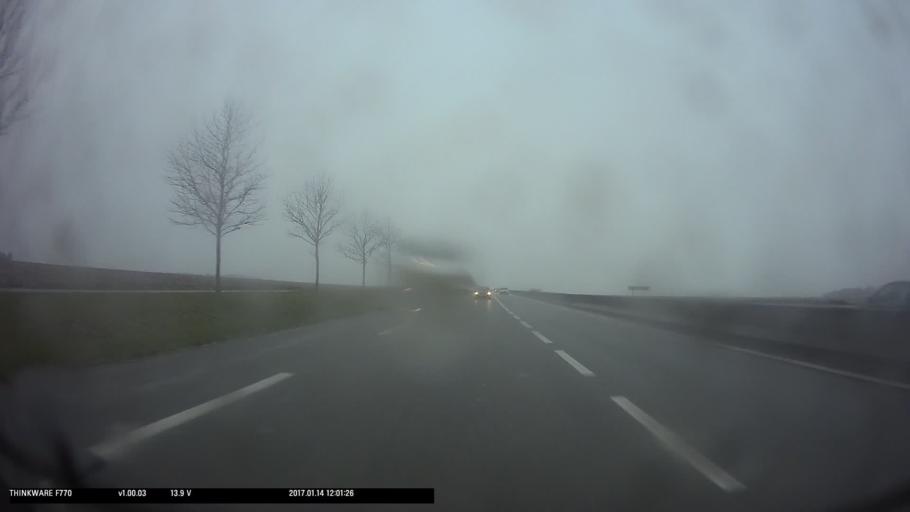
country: FR
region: Ile-de-France
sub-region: Departement du Val-d'Oise
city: Sagy
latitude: 49.0724
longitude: 1.9562
